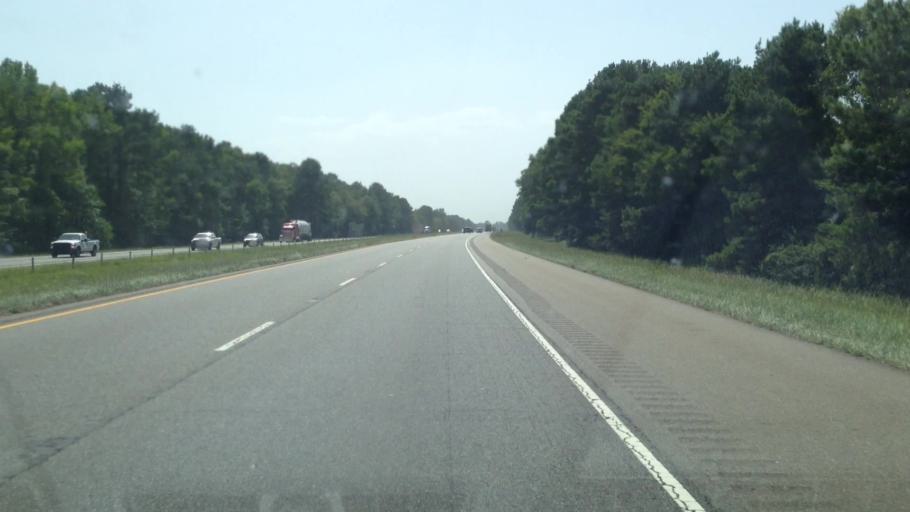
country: US
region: Louisiana
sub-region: Bossier Parish
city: Haughton
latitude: 32.5774
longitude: -93.4496
